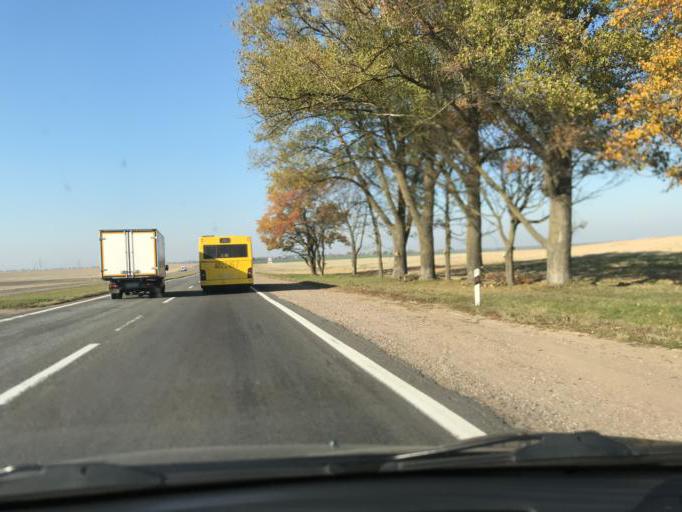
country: BY
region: Minsk
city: Dukora
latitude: 53.6874
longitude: 27.9097
